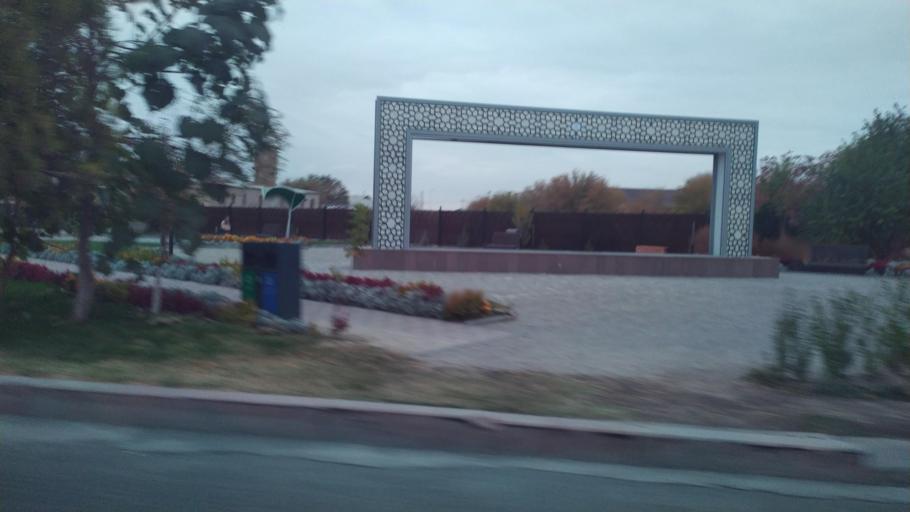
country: KZ
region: Ongtustik Qazaqstan
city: Turkestan
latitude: 43.2990
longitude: 68.2764
